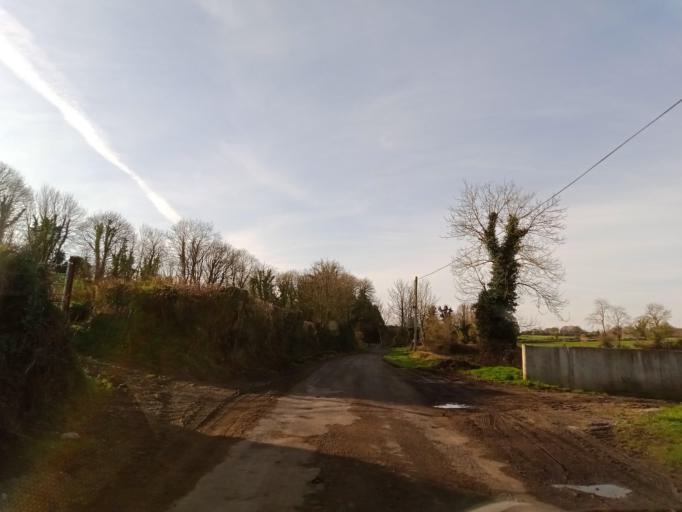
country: IE
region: Munster
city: Fethard
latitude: 52.5618
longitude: -7.5859
